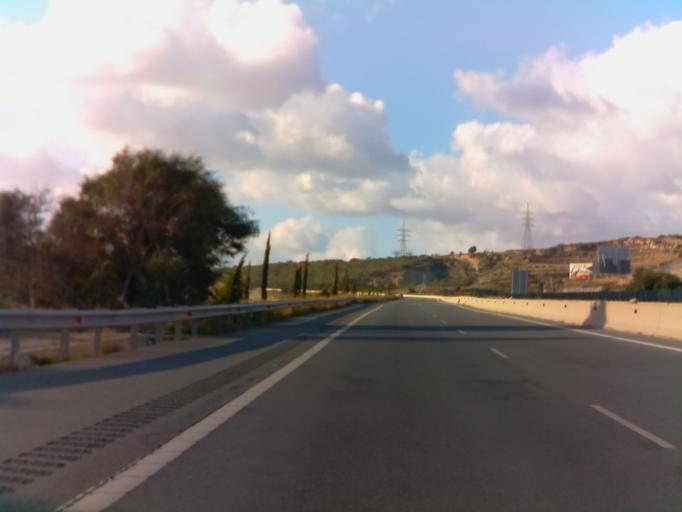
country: CY
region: Pafos
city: Mesogi
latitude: 34.7646
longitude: 32.4872
